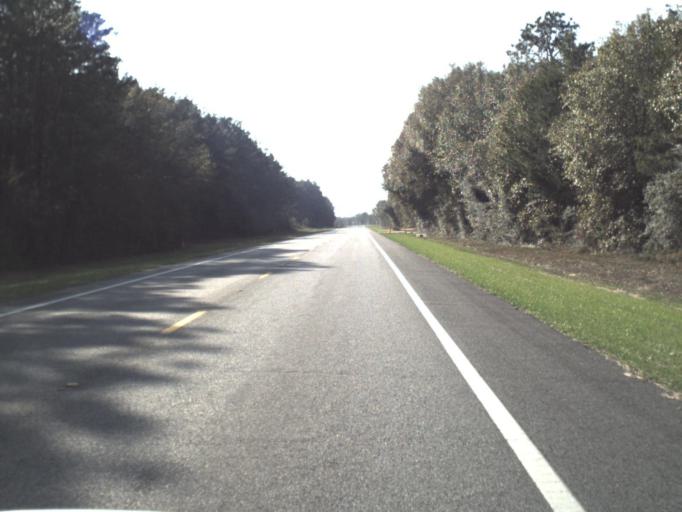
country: US
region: Florida
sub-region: Bay County
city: Youngstown
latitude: 30.4367
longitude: -85.5113
